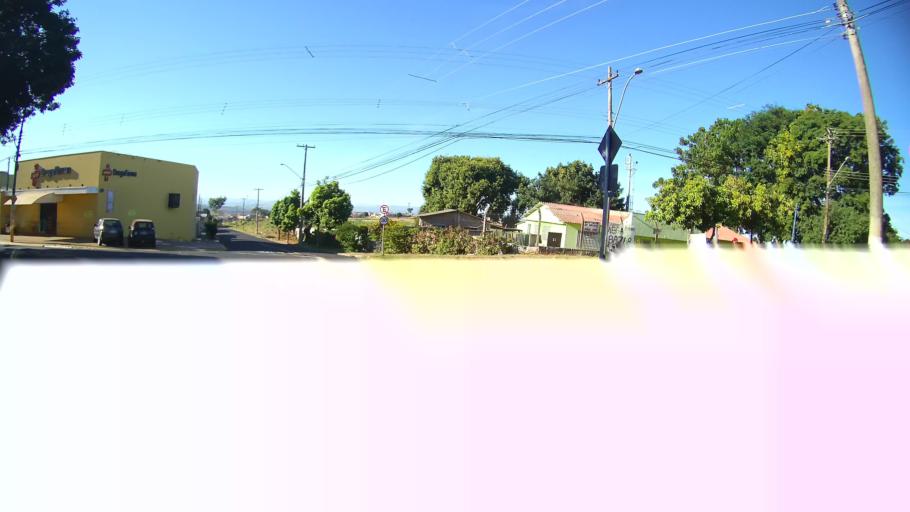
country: BR
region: Sao Paulo
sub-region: Franca
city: Franca
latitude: -20.5809
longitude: -47.3797
